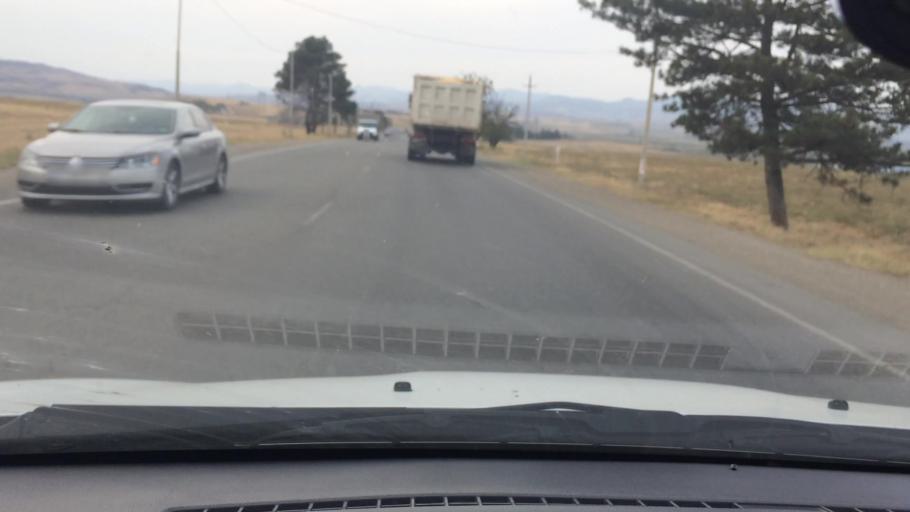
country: GE
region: Kvemo Kartli
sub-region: Marneuli
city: Marneuli
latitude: 41.5135
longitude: 44.7887
